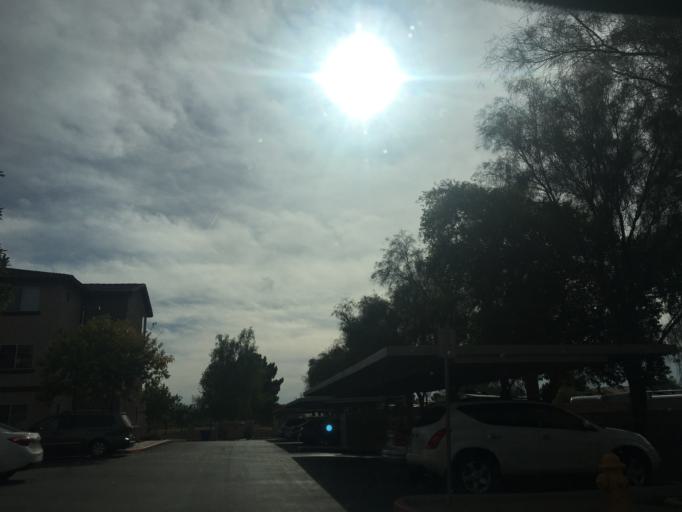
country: US
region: Arizona
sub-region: Maricopa County
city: Gilbert
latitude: 33.3533
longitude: -111.7944
